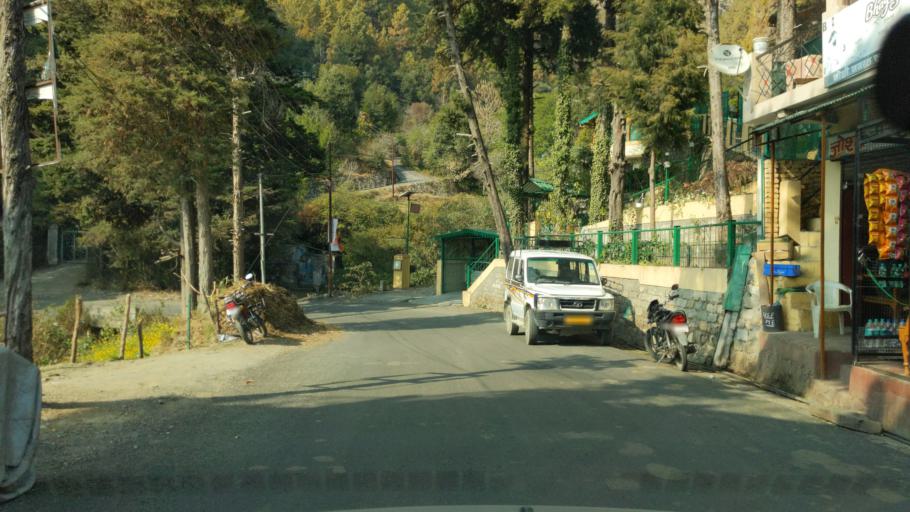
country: IN
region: Uttarakhand
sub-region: Naini Tal
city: Bhowali
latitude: 29.3922
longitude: 79.5333
